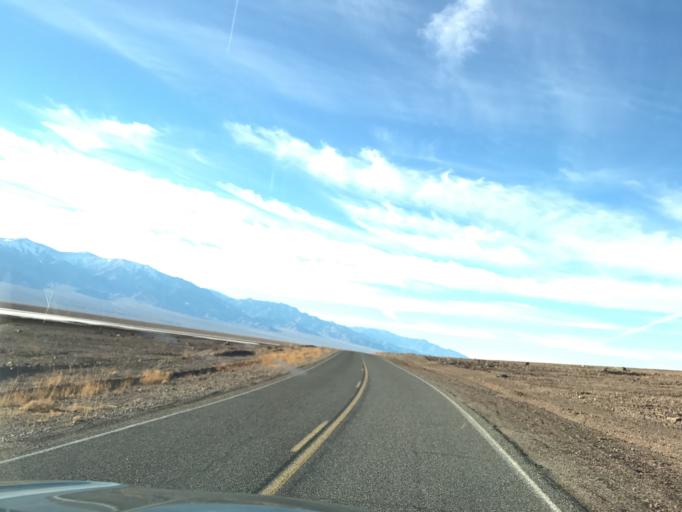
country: US
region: Nevada
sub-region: Nye County
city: Beatty
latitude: 36.1897
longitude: -116.7691
